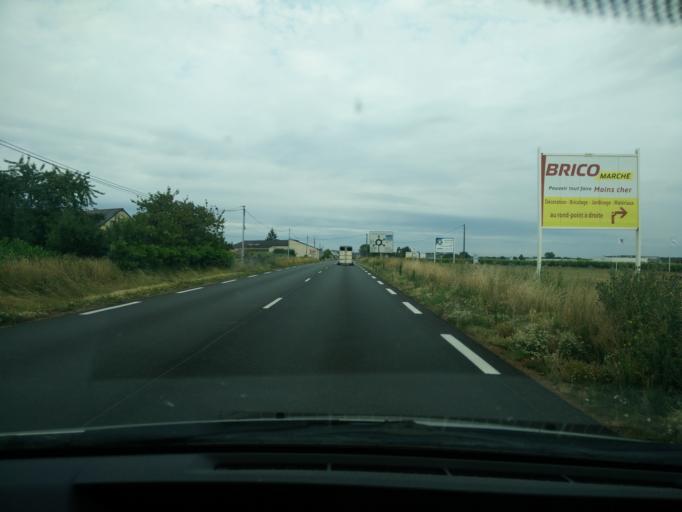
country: FR
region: Pays de la Loire
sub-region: Departement de Maine-et-Loire
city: Brissac-Quince
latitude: 47.3407
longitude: -0.4335
